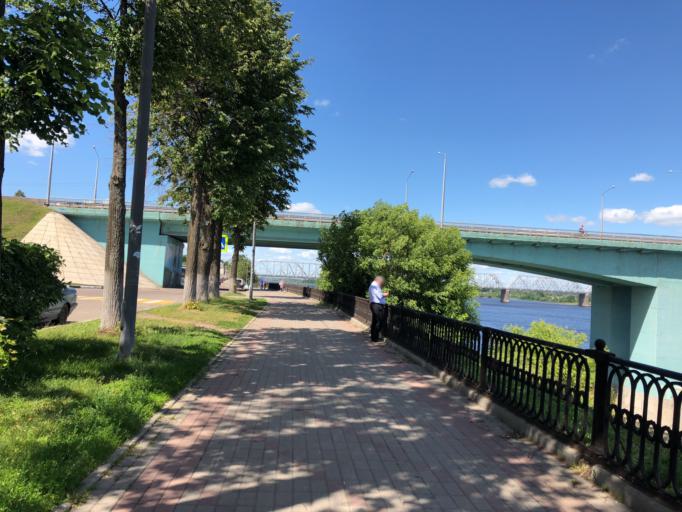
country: RU
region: Jaroslavl
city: Yaroslavl
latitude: 57.6388
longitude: 39.8889
